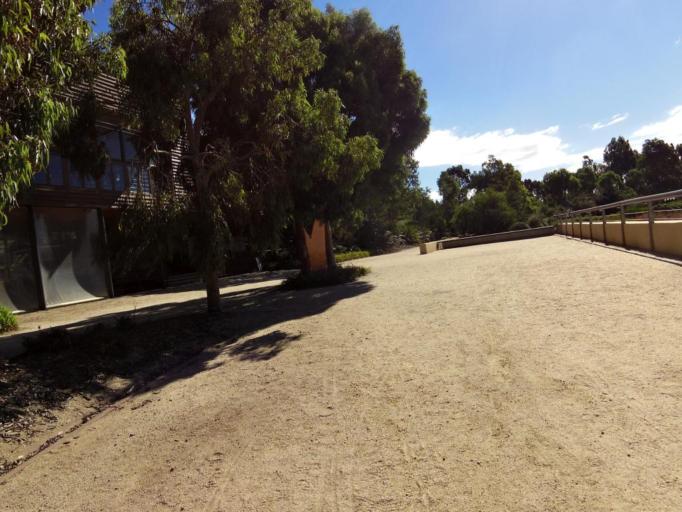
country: AU
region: Victoria
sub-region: Casey
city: Botanic Ridge
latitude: -38.1303
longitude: 145.2697
